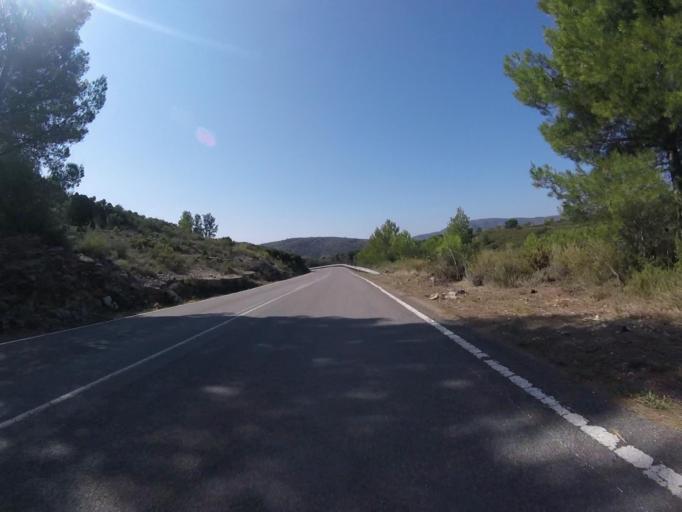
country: ES
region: Valencia
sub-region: Provincia de Castello
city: Benafigos
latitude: 40.2543
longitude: -0.2127
